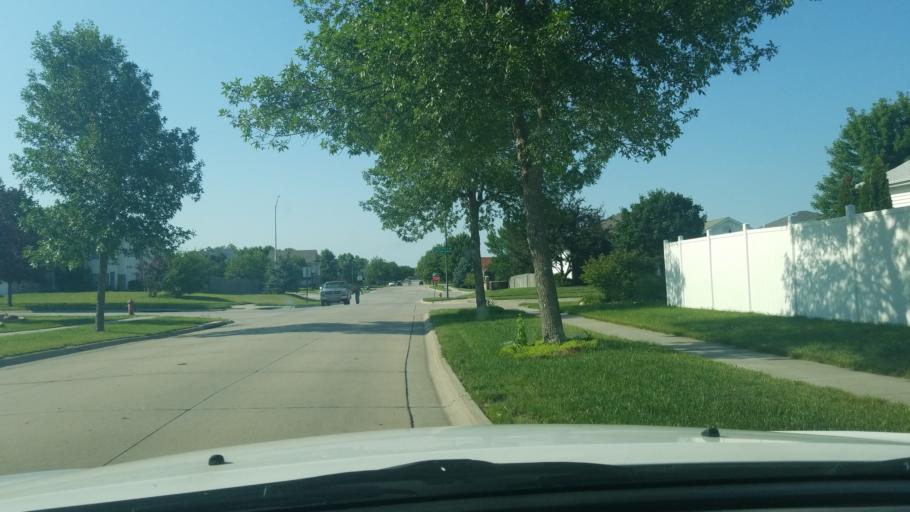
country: US
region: Nebraska
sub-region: Lancaster County
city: Lincoln
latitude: 40.7543
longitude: -96.6125
